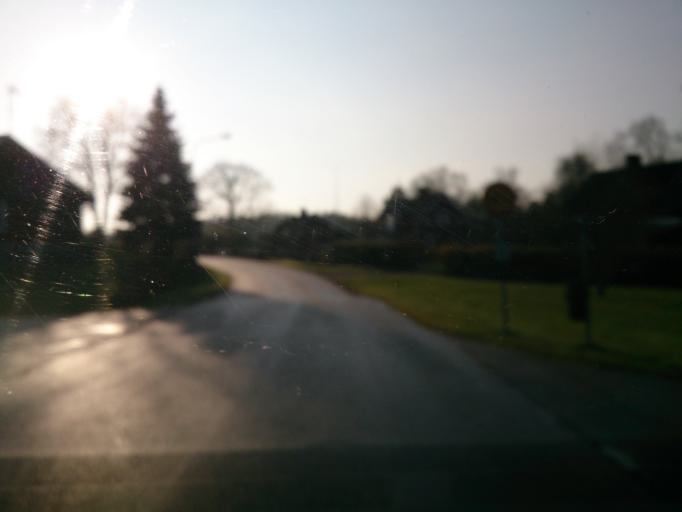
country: SE
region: OEstergoetland
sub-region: Atvidabergs Kommun
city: Atvidaberg
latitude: 58.3330
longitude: 16.0225
